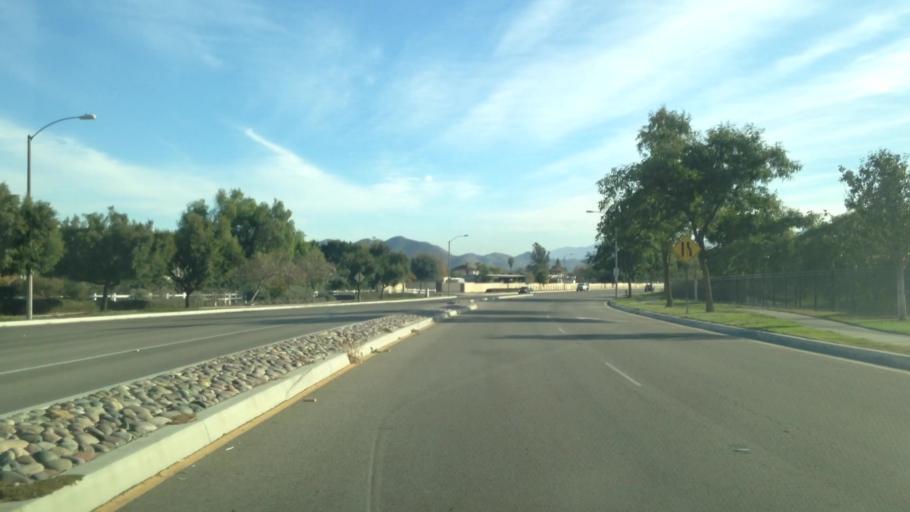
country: US
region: California
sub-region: Riverside County
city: Mira Loma
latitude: 33.9933
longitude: -117.5412
